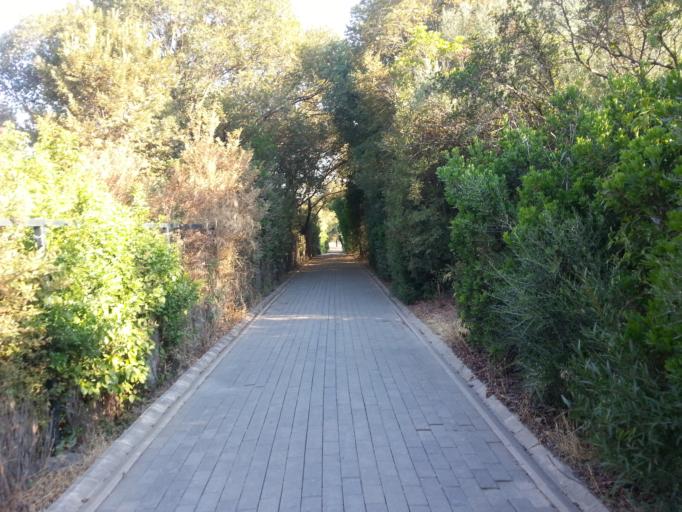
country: ES
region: Andalusia
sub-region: Provincia de Sevilla
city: Sevilla
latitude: 37.4167
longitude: -5.9946
